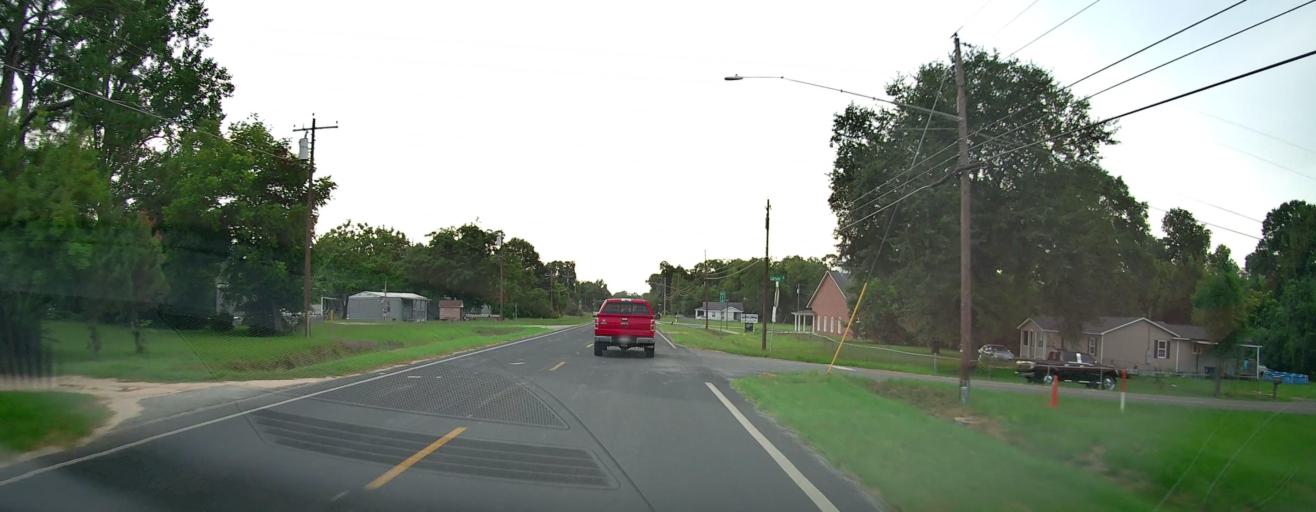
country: US
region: Georgia
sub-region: Laurens County
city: East Dublin
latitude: 32.5393
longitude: -82.8543
